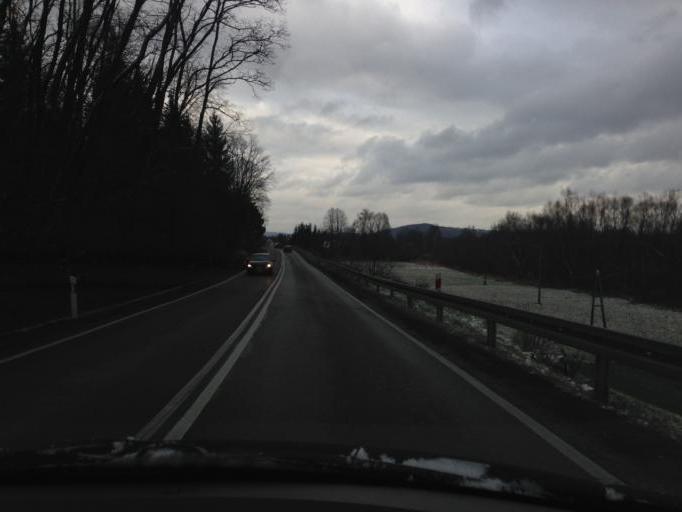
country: PL
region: Lesser Poland Voivodeship
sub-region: Powiat myslenicki
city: Dobczyce
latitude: 49.9003
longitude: 20.1259
